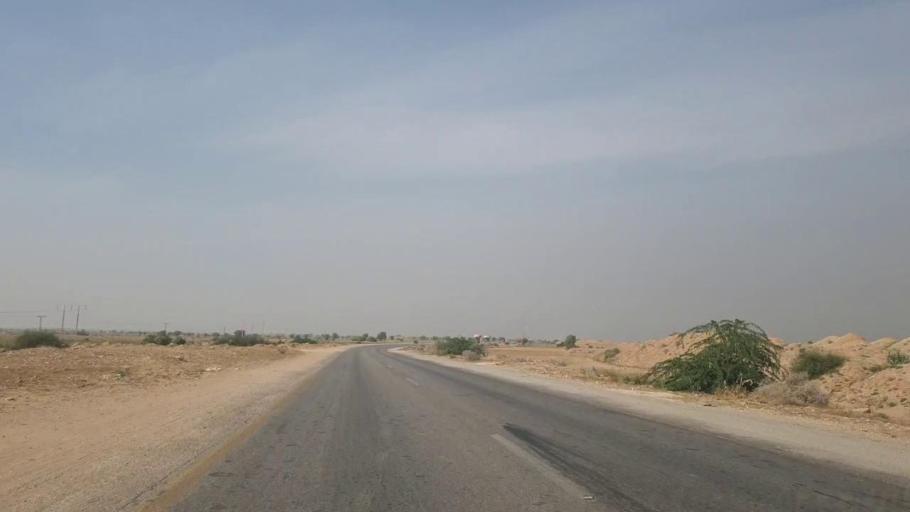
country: PK
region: Sindh
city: Sann
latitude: 26.0397
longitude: 68.1140
